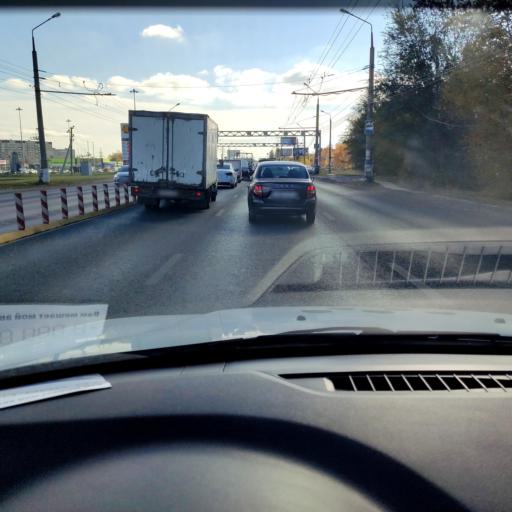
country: RU
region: Samara
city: Tol'yatti
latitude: 53.5418
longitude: 49.3854
